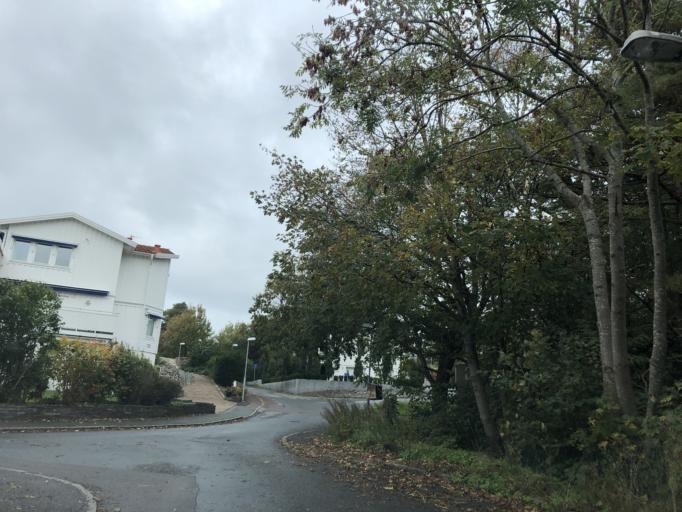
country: SE
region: Vaestra Goetaland
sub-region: Goteborg
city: Majorna
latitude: 57.6718
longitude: 11.8550
